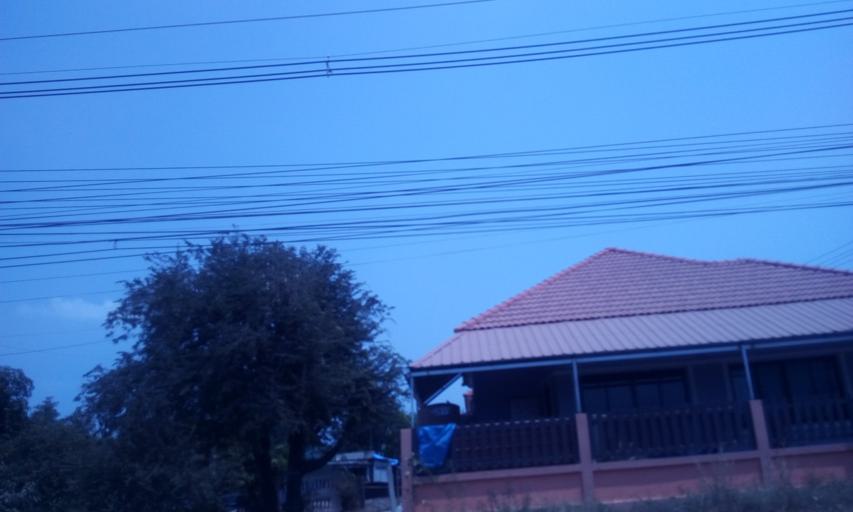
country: TH
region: Chachoengsao
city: Bang Nam Priao
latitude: 13.7737
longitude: 101.0653
